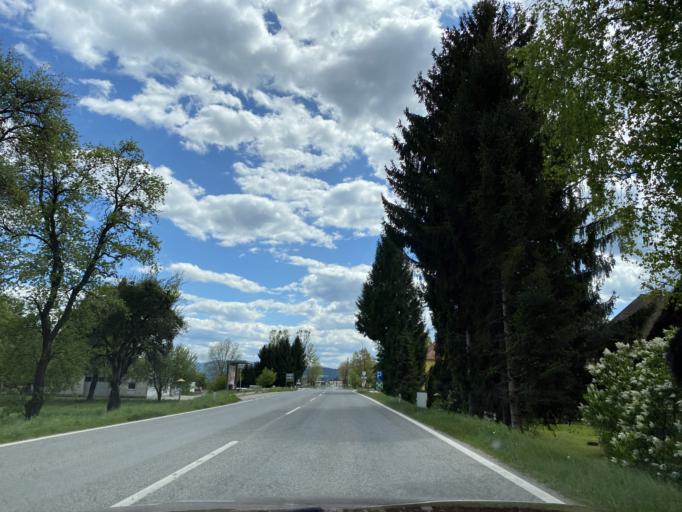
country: AT
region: Carinthia
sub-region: Politischer Bezirk Wolfsberg
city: Sankt Andrae
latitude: 46.7906
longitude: 14.8254
